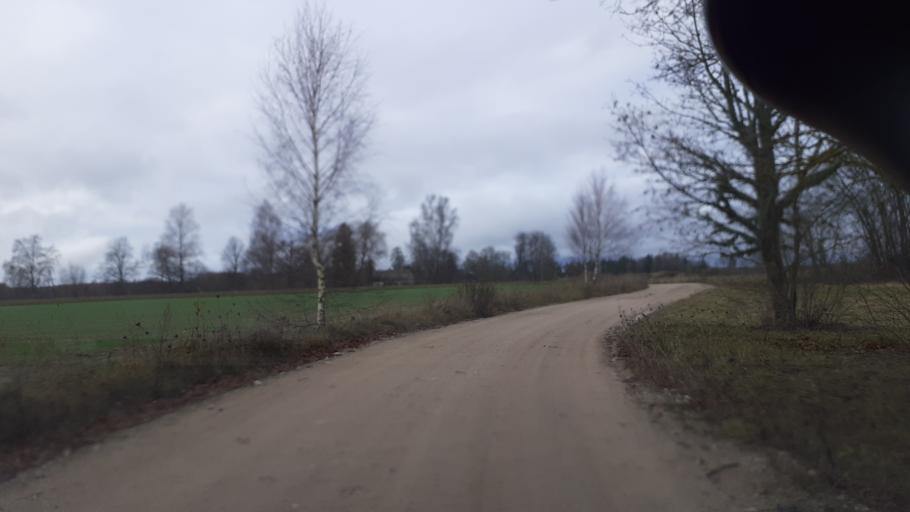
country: LV
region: Kuldigas Rajons
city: Kuldiga
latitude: 57.0433
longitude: 21.8720
